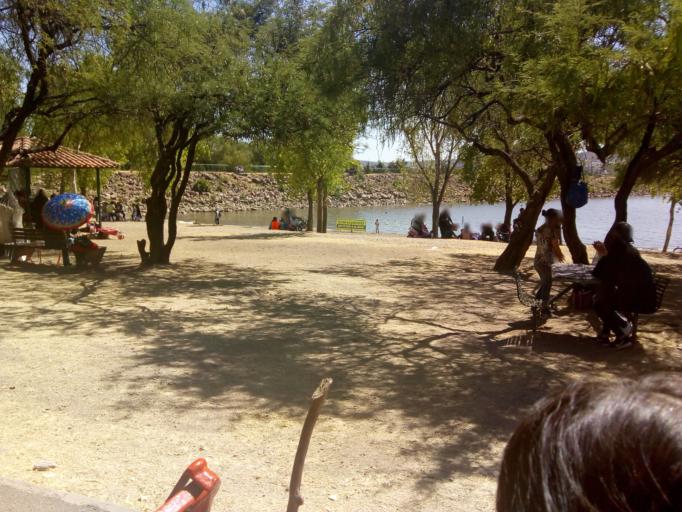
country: MX
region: Guanajuato
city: Leon
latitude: 21.1742
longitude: -101.6791
